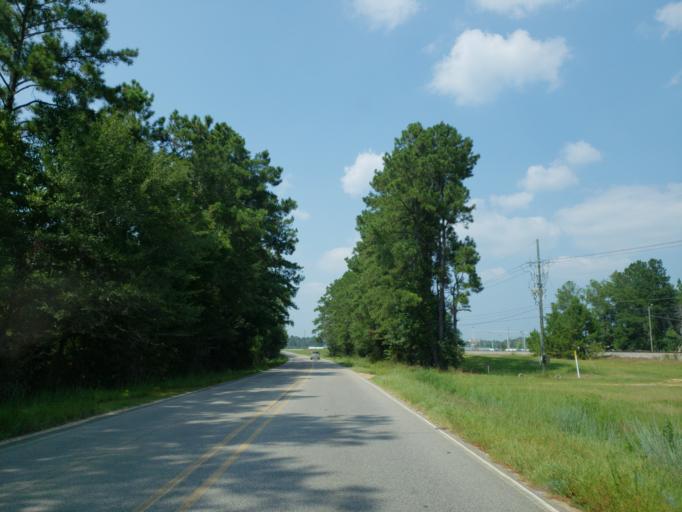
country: US
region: Mississippi
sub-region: Forrest County
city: Petal
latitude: 31.3777
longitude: -89.2676
